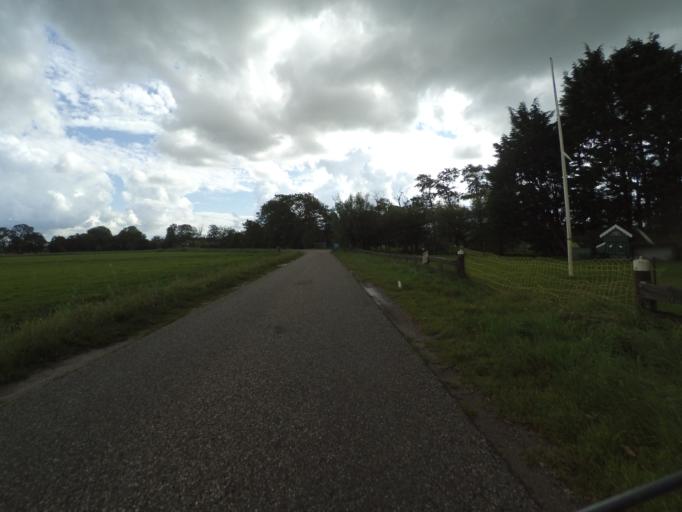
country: NL
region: North Holland
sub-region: Gemeente Alkmaar
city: Alkmaar
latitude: 52.6469
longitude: 4.7154
